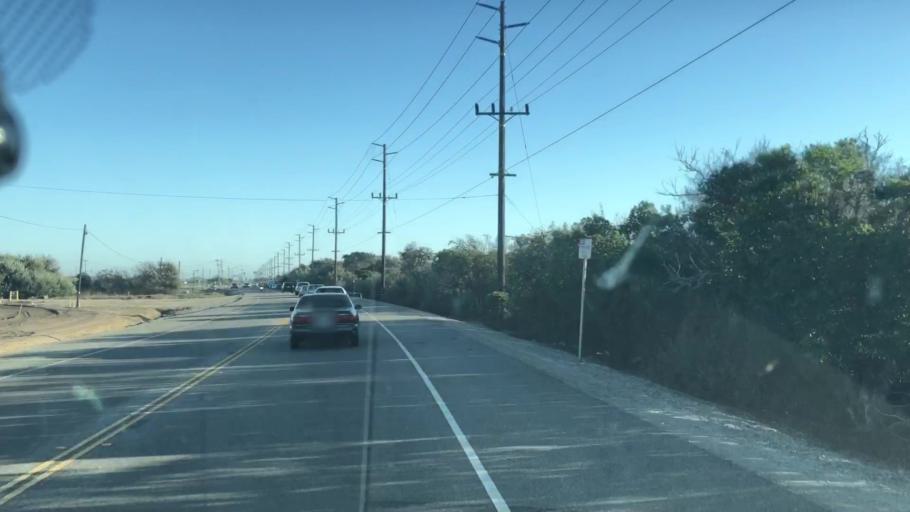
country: US
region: California
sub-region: Ventura County
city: Oxnard Shores
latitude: 34.2221
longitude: -119.2557
